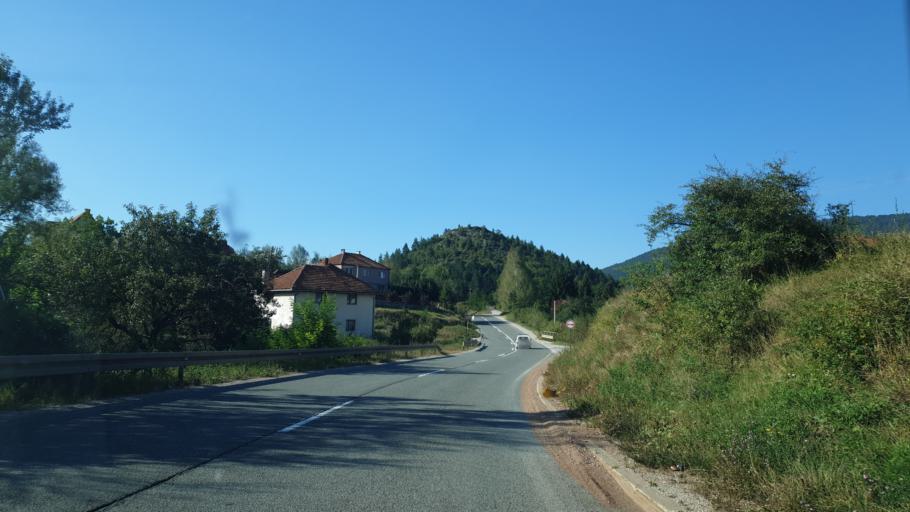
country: RS
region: Central Serbia
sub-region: Zlatiborski Okrug
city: Nova Varos
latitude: 43.5428
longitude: 19.7876
